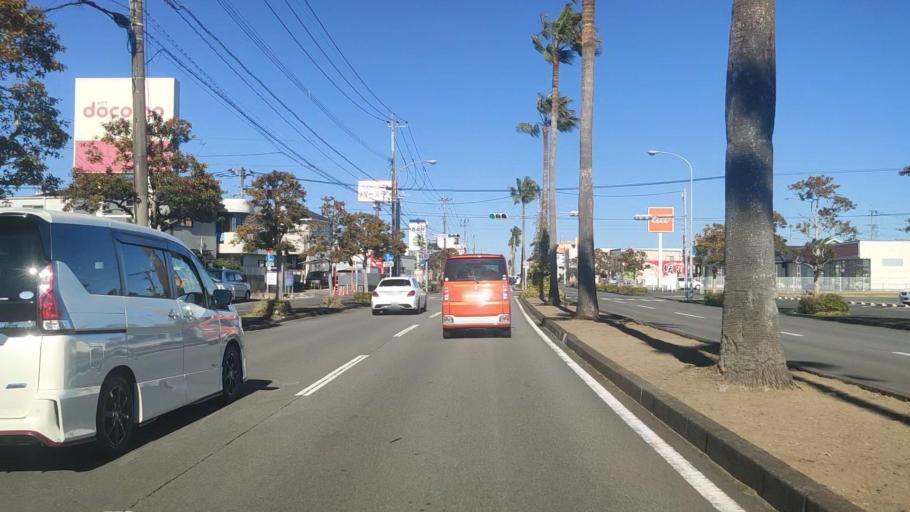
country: JP
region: Miyazaki
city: Miyazaki-shi
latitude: 31.9121
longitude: 131.4477
